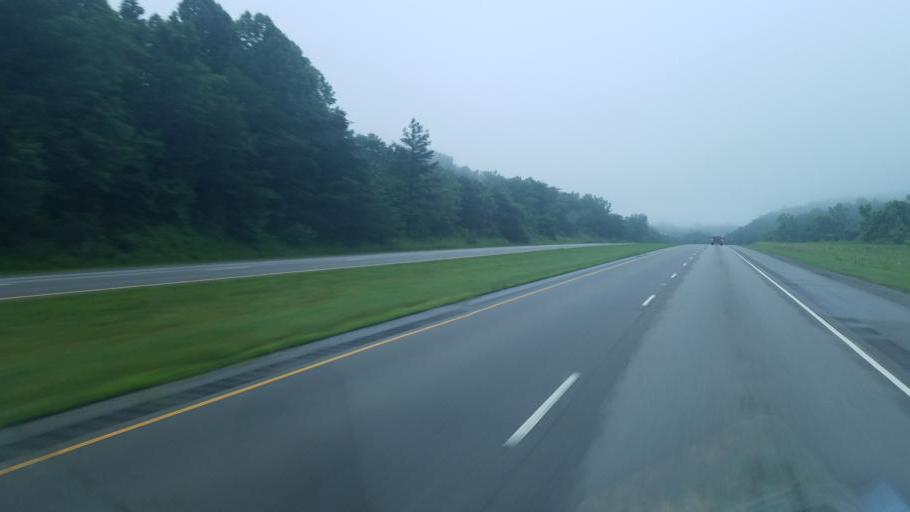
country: US
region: Ohio
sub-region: Jackson County
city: Oak Hill
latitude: 38.9426
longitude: -82.4742
